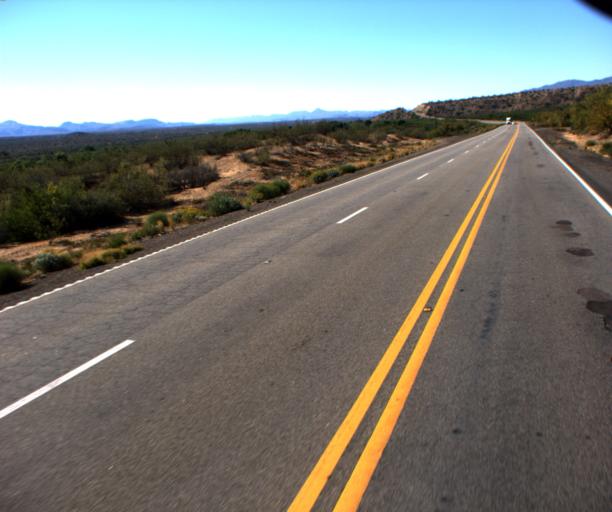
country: US
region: Arizona
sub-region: Yavapai County
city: Bagdad
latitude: 34.8072
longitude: -113.6260
